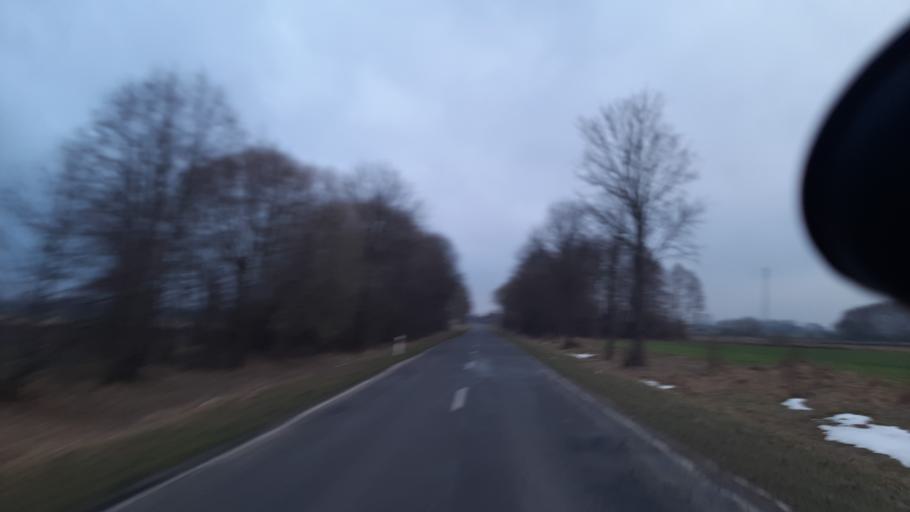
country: PL
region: Lublin Voivodeship
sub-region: Powiat parczewski
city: Debowa Kloda
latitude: 51.6183
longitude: 23.1005
